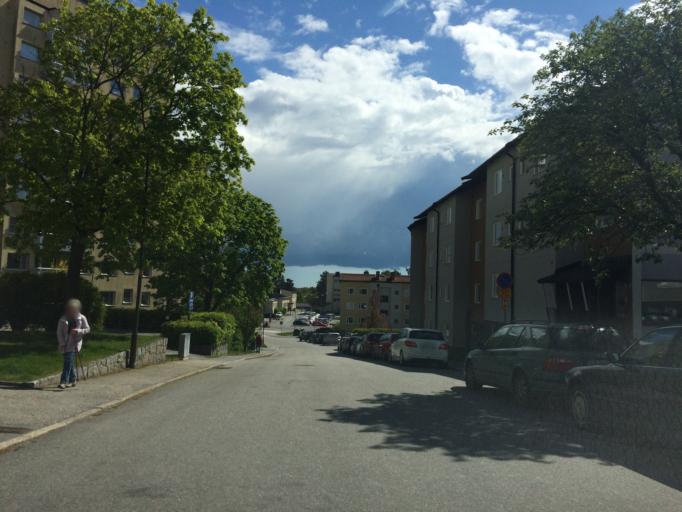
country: SE
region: Stockholm
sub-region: Huddinge Kommun
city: Segeltorp
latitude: 59.2863
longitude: 17.9607
